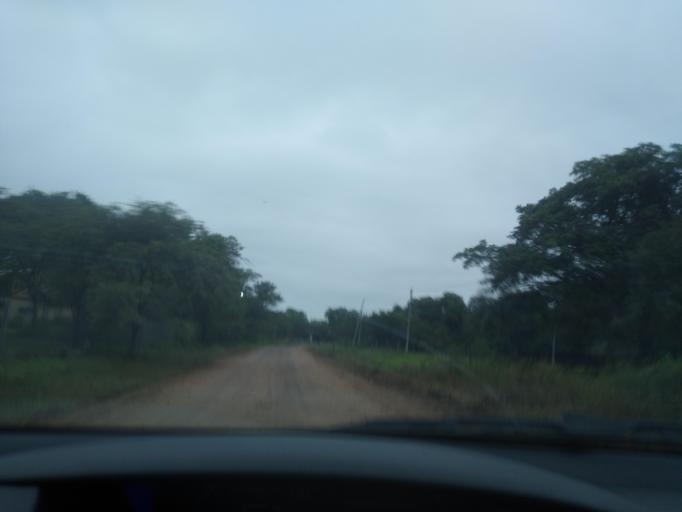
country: AR
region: Chaco
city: Colonia Benitez
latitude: -27.3321
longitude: -58.9644
